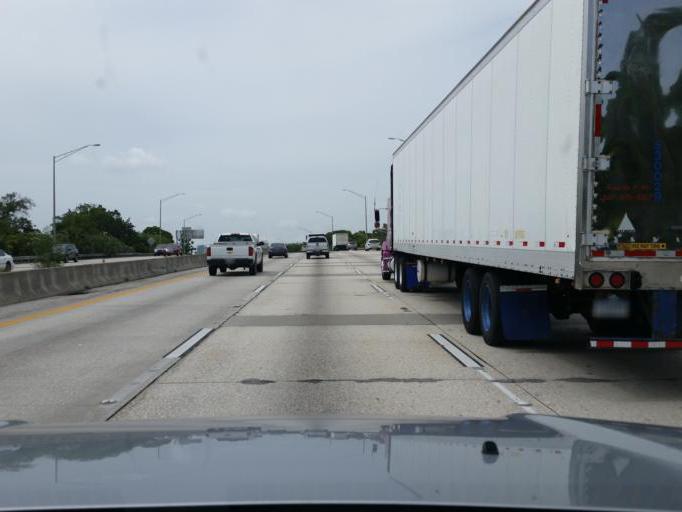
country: US
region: Florida
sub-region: Orange County
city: Fairview Shores
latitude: 28.5769
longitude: -81.3754
